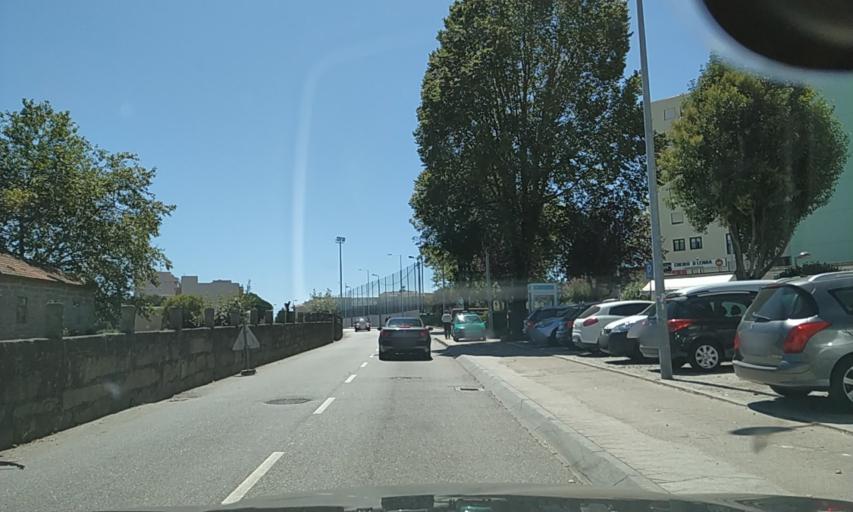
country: PT
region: Porto
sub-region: Vila Nova de Gaia
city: Canidelo
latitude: 41.1339
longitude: -8.6452
